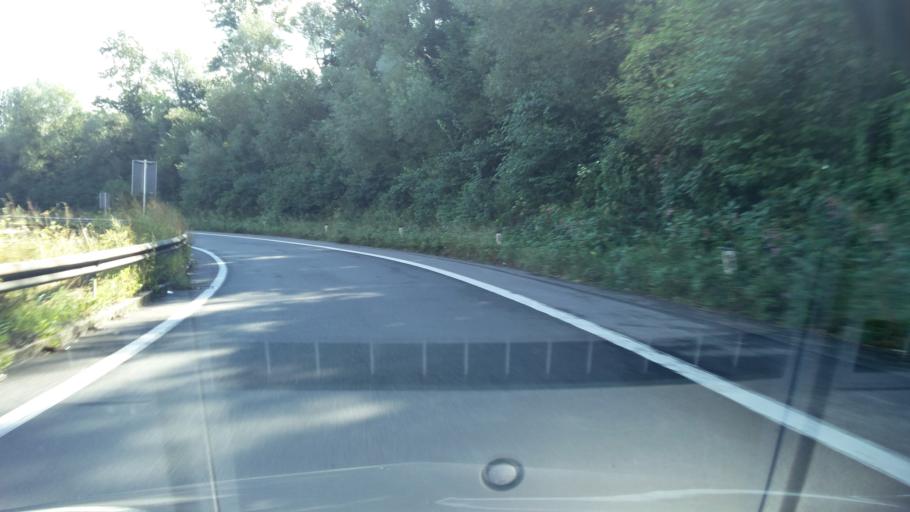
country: AT
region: Styria
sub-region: Politischer Bezirk Weiz
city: Gleisdorf
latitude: 47.0972
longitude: 15.6878
